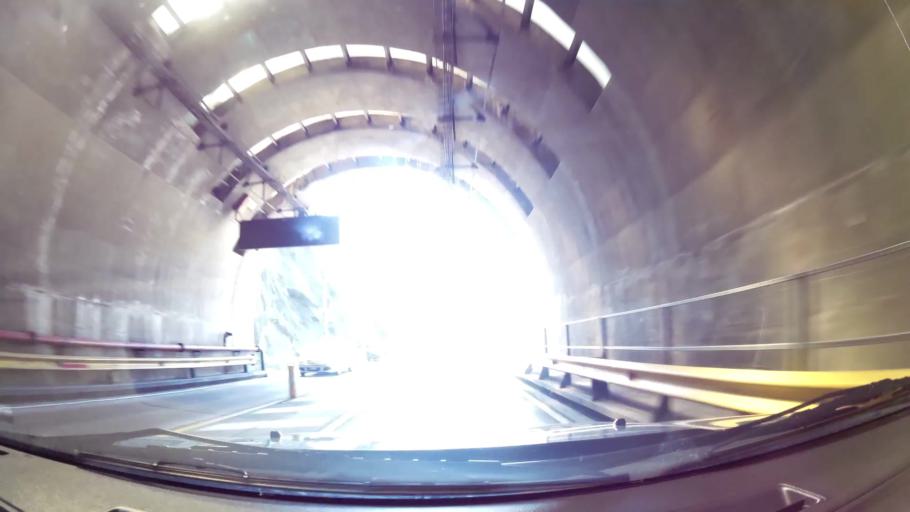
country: EC
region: Pichincha
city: Quito
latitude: -0.1936
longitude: -78.4668
